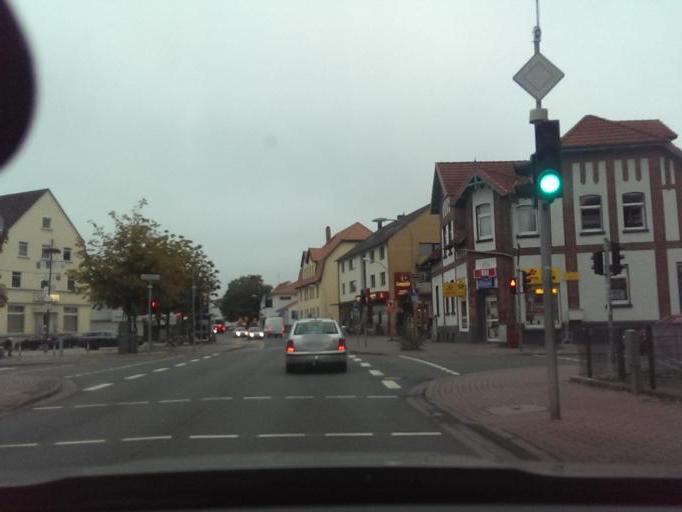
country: DE
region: Lower Saxony
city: Garbsen
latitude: 52.4136
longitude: 9.5882
